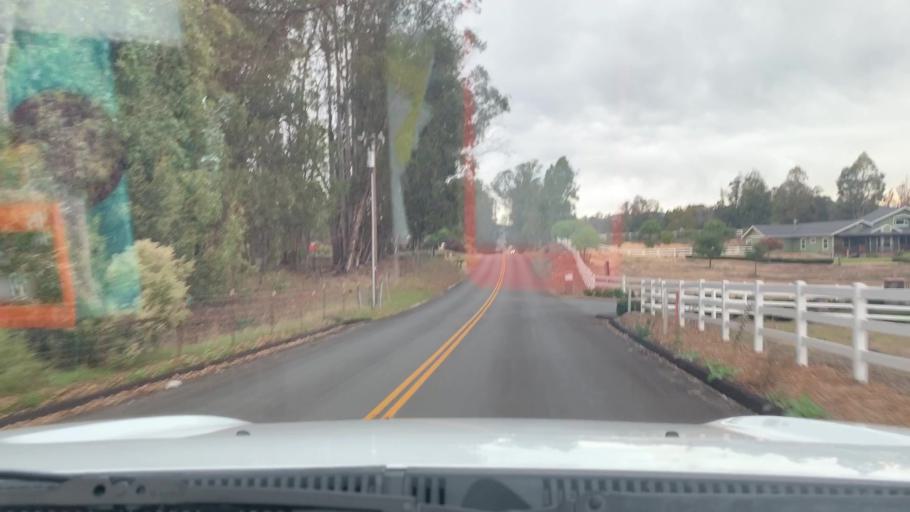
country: US
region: California
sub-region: San Luis Obispo County
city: Callender
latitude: 35.0674
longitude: -120.5551
